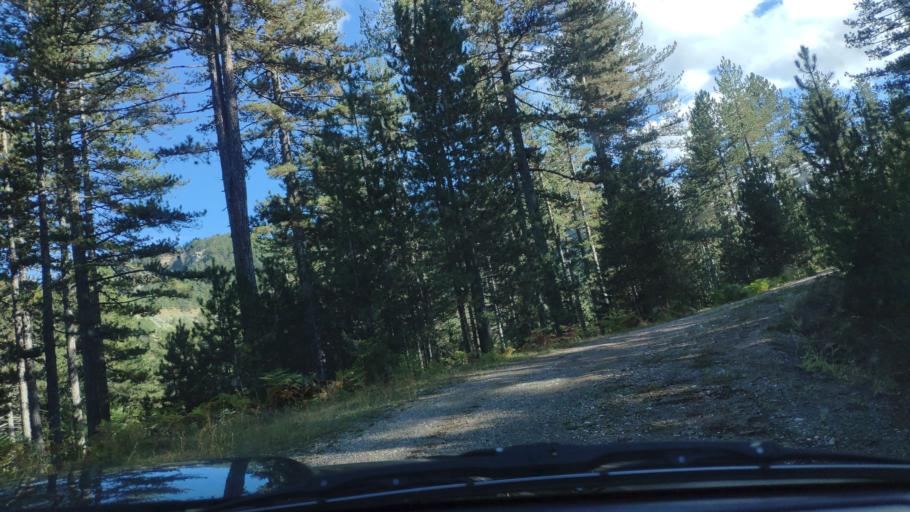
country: AL
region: Korce
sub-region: Rrethi i Devollit
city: Miras
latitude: 40.3937
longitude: 20.8866
